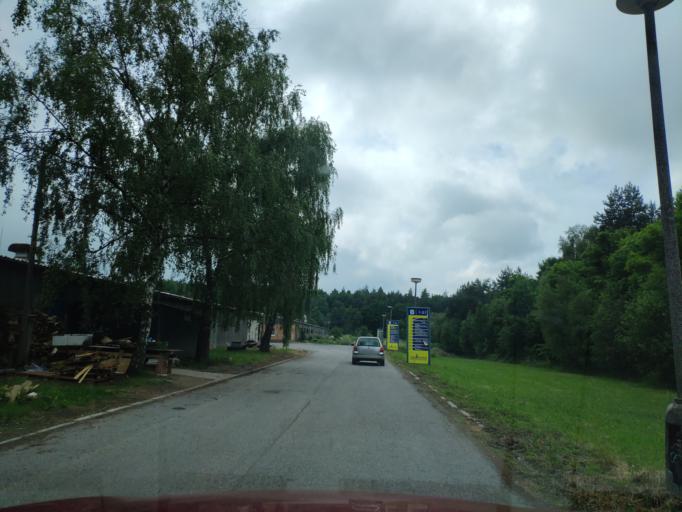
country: SK
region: Presovsky
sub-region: Okres Presov
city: Presov
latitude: 48.9986
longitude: 21.3193
